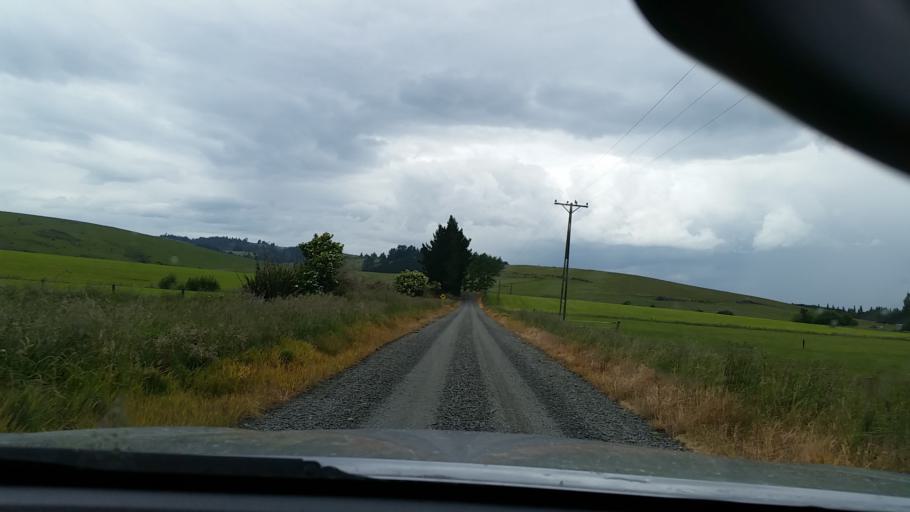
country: NZ
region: Southland
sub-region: Southland District
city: Winton
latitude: -45.9698
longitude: 168.1406
